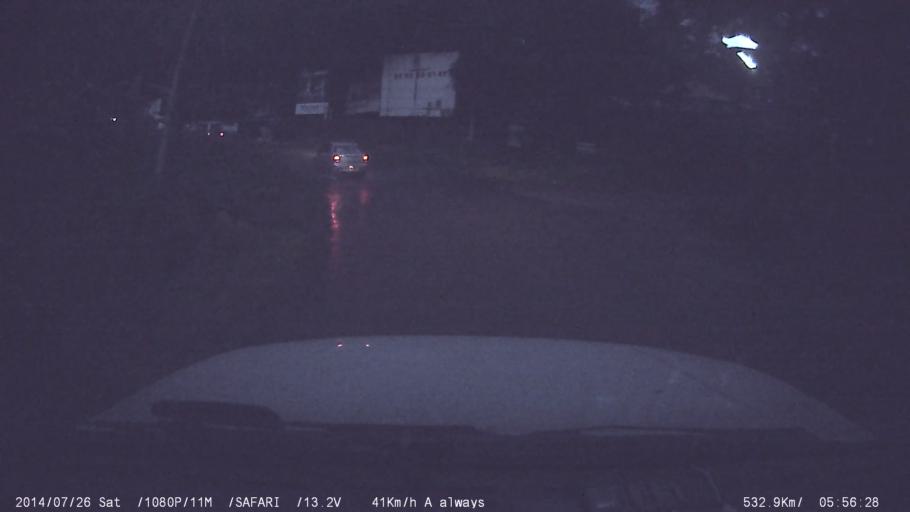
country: IN
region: Kerala
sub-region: Ernakulam
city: Muvattupuzha
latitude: 9.9331
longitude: 76.5740
